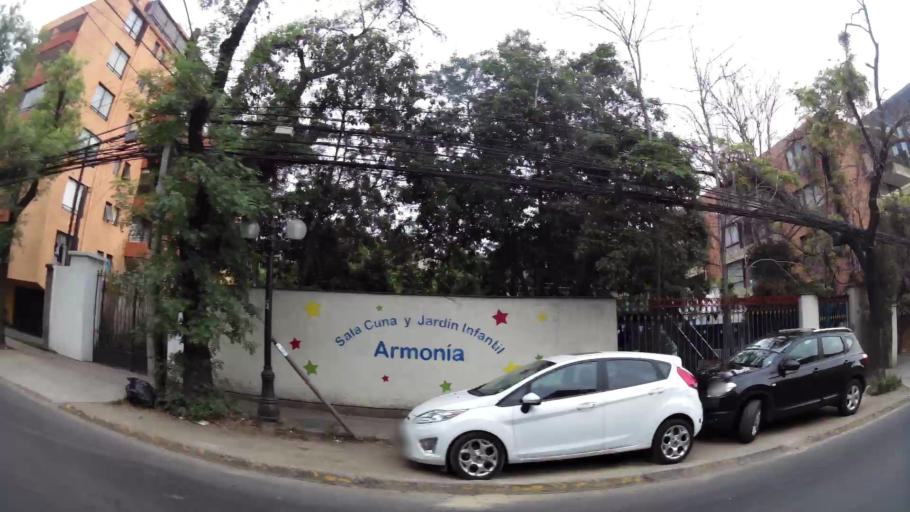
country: CL
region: Santiago Metropolitan
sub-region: Provincia de Santiago
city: Villa Presidente Frei, Nunoa, Santiago, Chile
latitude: -33.4286
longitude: -70.6094
